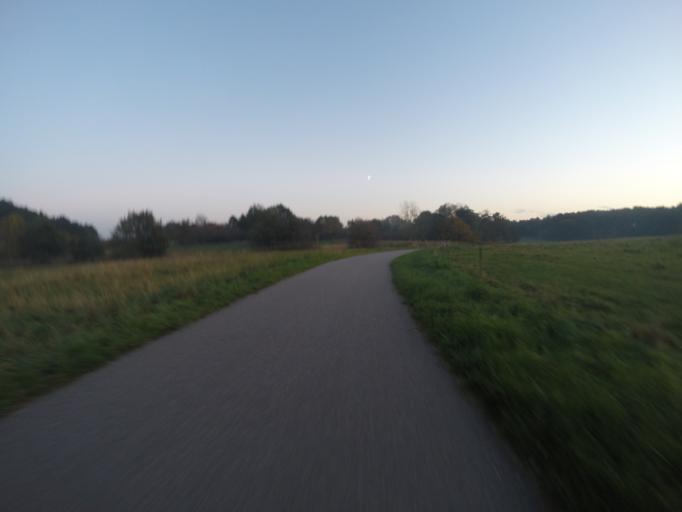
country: DK
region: Capital Region
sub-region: Albertslund Kommune
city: Albertslund
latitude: 55.6467
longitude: 12.3378
